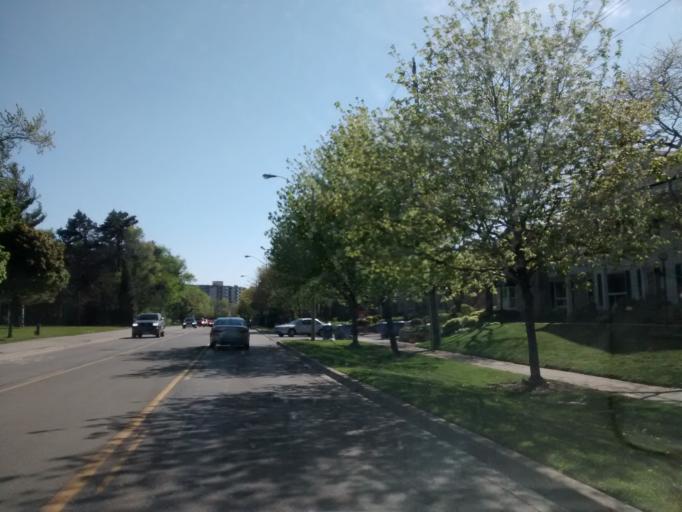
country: CA
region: Ontario
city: Oakville
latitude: 43.3709
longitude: -79.7262
